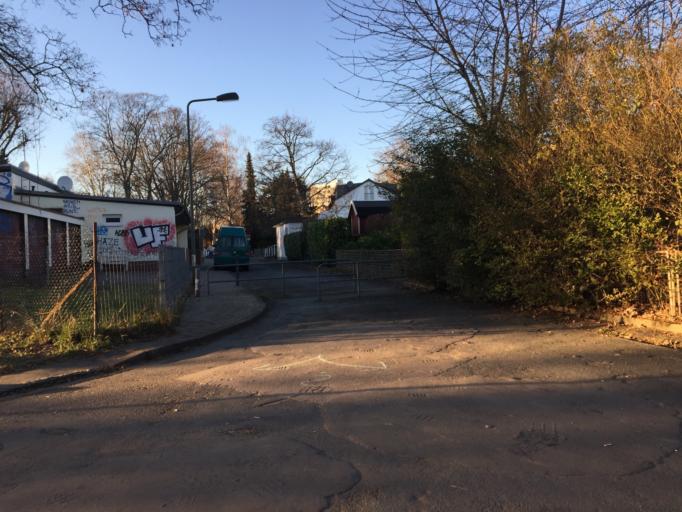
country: DE
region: Hesse
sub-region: Regierungsbezirk Darmstadt
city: Frankfurt am Main
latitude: 50.1586
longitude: 8.6626
